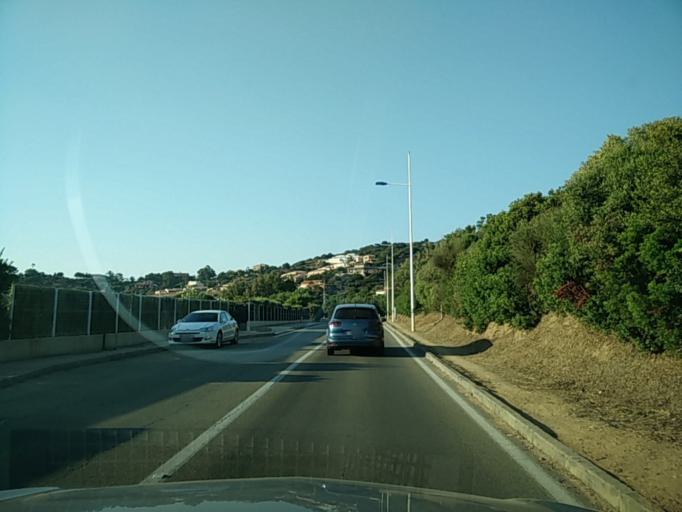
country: FR
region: Corsica
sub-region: Departement de la Corse-du-Sud
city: Pietrosella
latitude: 41.8702
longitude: 8.7873
